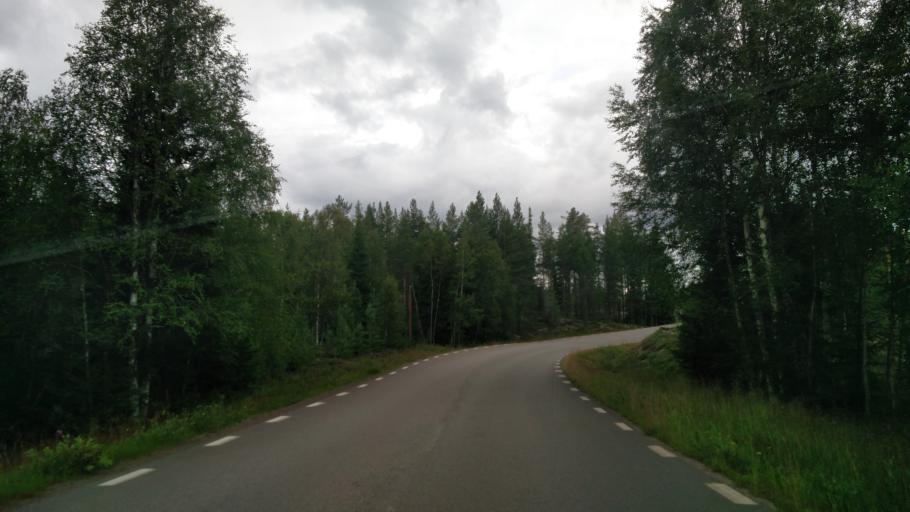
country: NO
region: Hedmark
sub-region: Trysil
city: Innbygda
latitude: 61.1551
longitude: 12.8131
